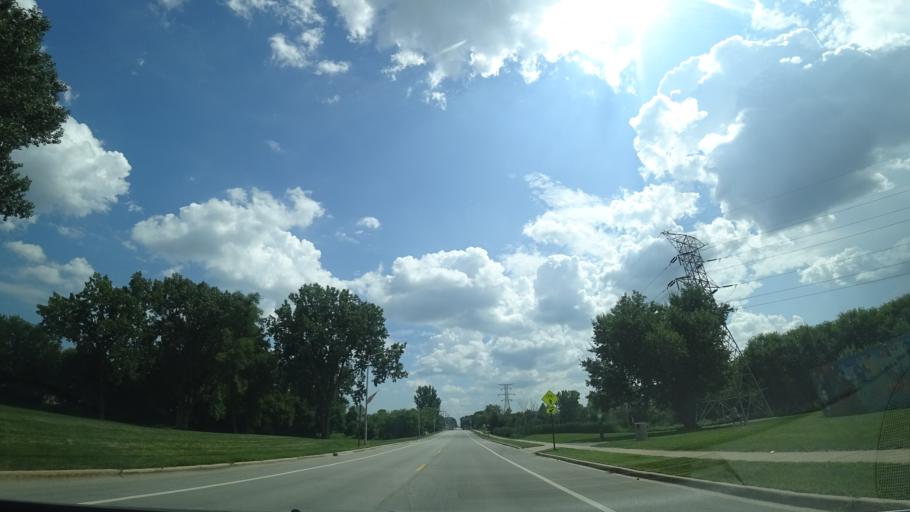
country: US
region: Illinois
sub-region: Cook County
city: Alsip
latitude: 41.6737
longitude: -87.7294
